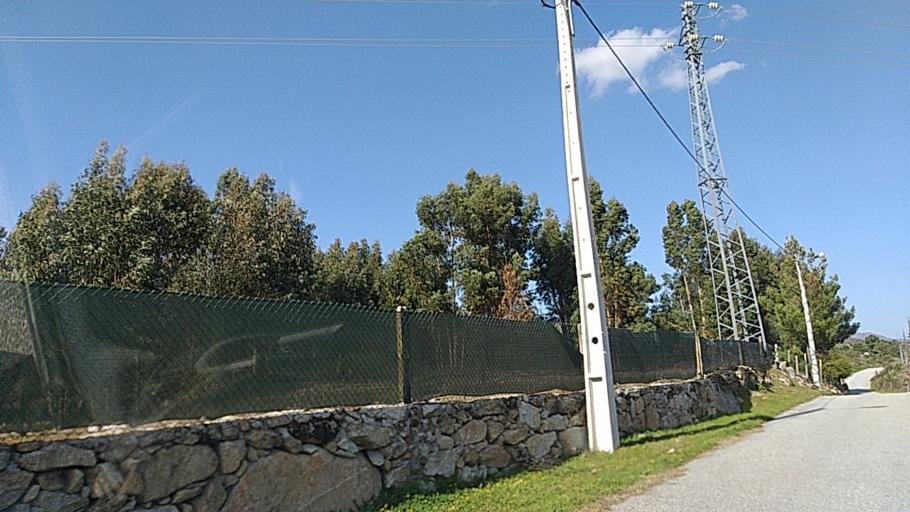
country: PT
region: Guarda
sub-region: Celorico da Beira
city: Celorico da Beira
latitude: 40.6386
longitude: -7.4321
